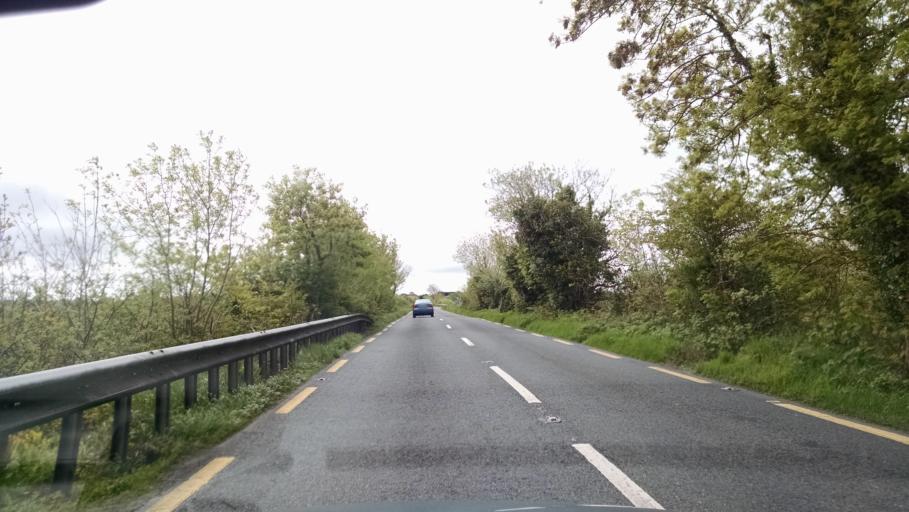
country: IE
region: Connaught
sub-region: County Galway
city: Claregalway
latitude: 53.3873
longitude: -9.0167
